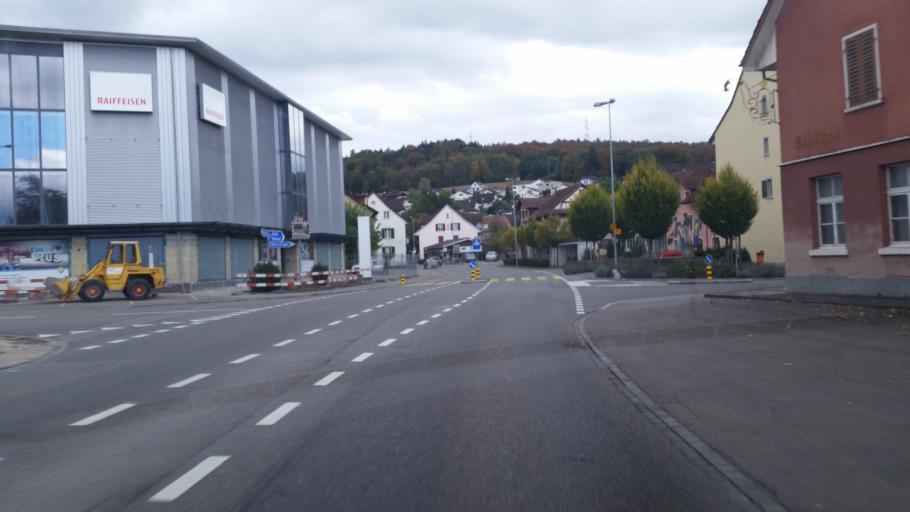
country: CH
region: Aargau
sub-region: Bezirk Zurzach
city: Oberendingen
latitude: 47.5384
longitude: 8.2902
